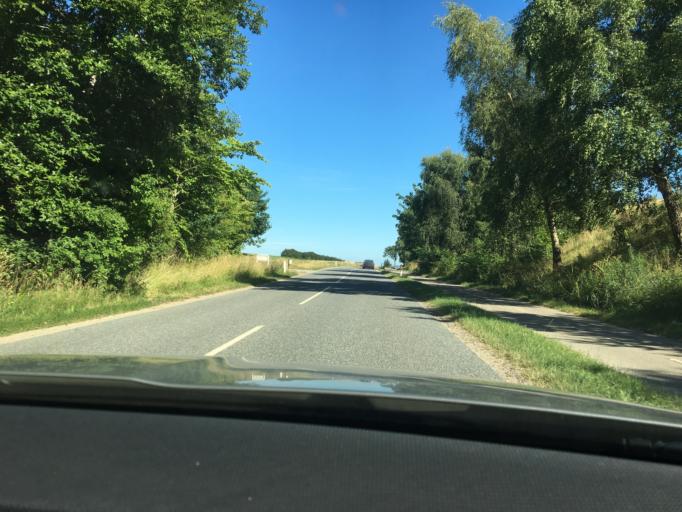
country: DK
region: Central Jutland
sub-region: Syddjurs Kommune
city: Hornslet
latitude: 56.3046
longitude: 10.3547
